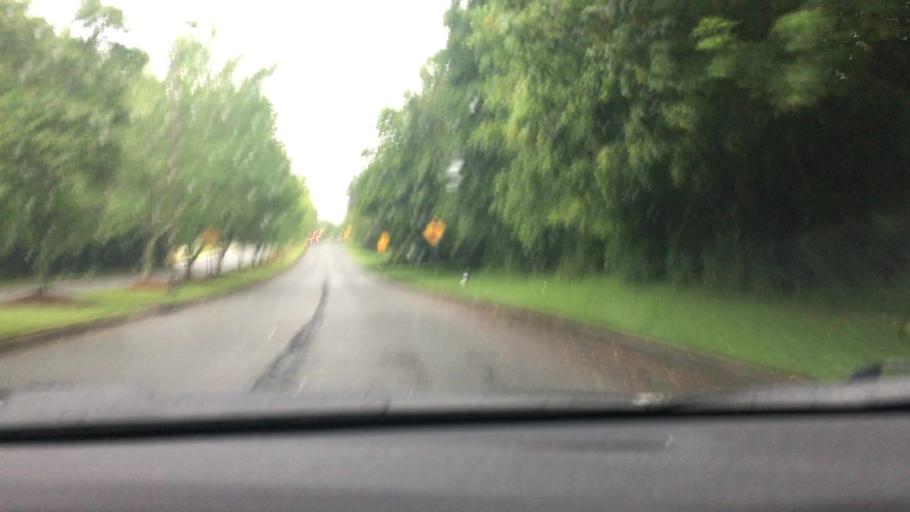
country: US
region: Georgia
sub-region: Fulton County
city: Union City
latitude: 33.6526
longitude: -84.5212
